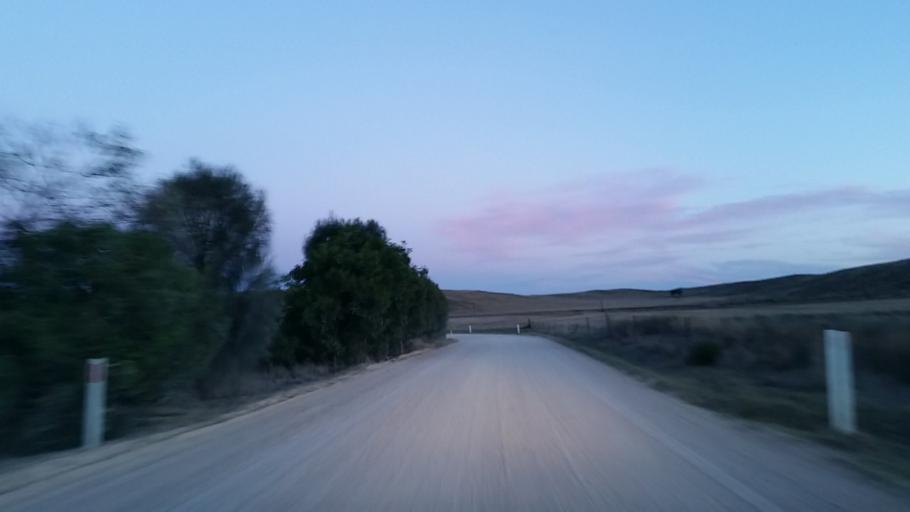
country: AU
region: South Australia
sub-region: Mount Barker
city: Callington
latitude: -35.1041
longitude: 139.0052
